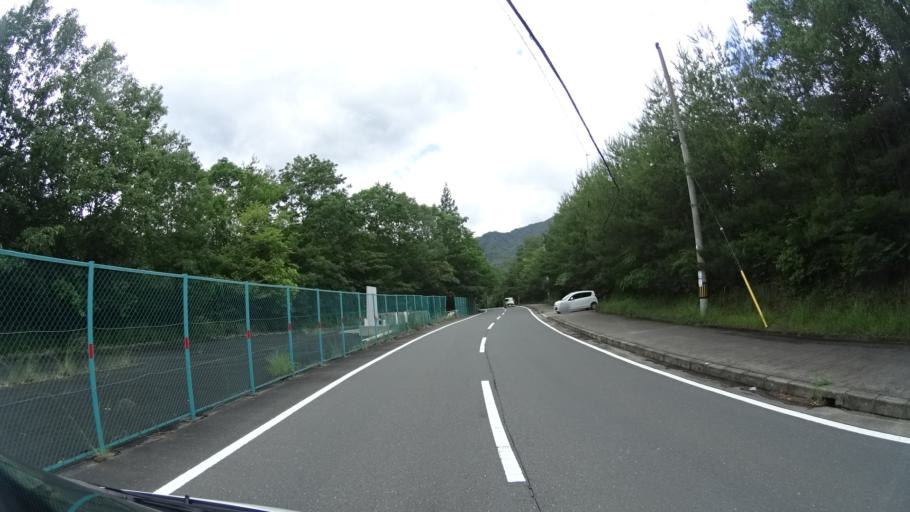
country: JP
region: Kyoto
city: Kameoka
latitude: 35.0125
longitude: 135.4354
